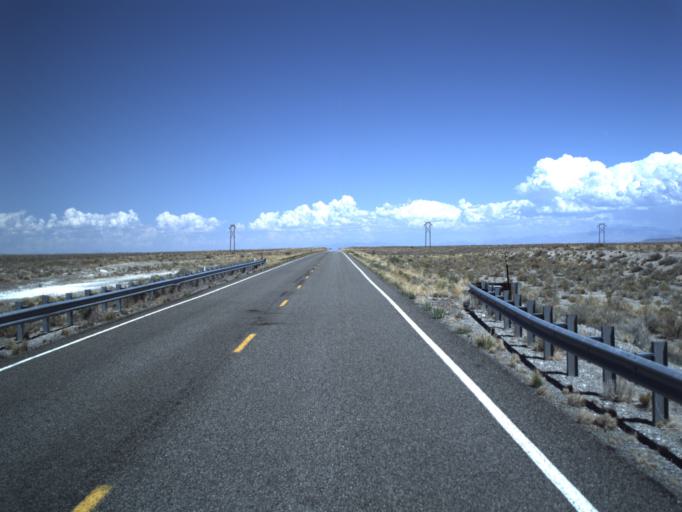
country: US
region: Utah
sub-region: Millard County
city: Delta
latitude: 39.1691
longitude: -113.0369
